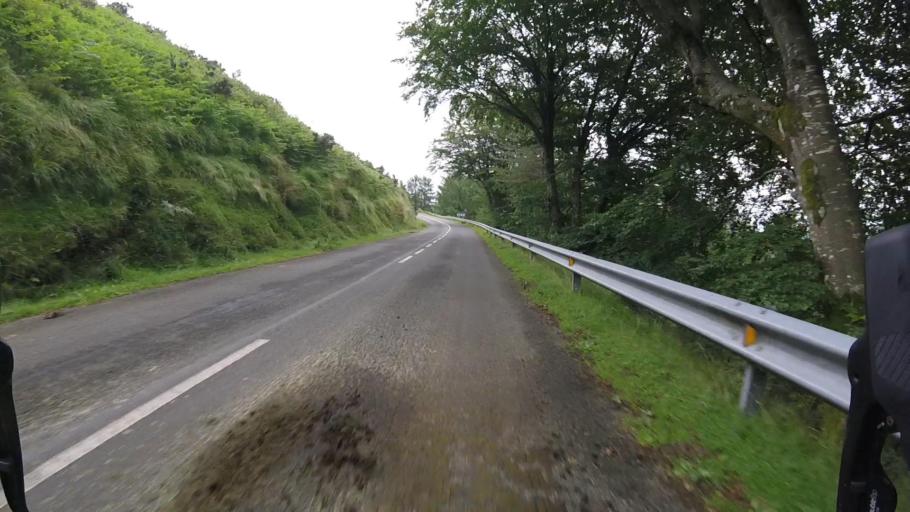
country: ES
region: Navarre
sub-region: Provincia de Navarra
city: Goizueta
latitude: 43.2434
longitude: -1.8098
